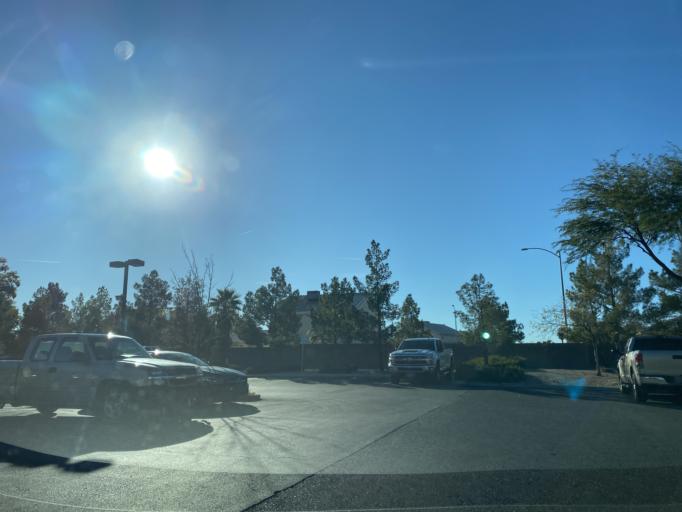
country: US
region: Nevada
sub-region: Clark County
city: Las Vegas
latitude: 36.2734
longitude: -115.2560
